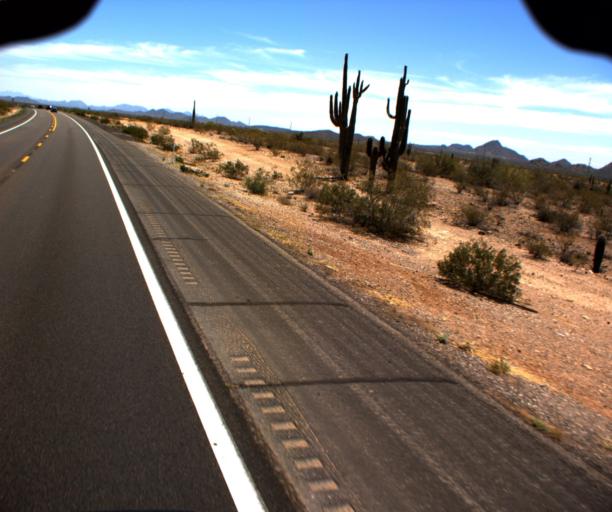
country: US
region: Arizona
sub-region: Maricopa County
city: Anthem
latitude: 33.7984
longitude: -112.2292
